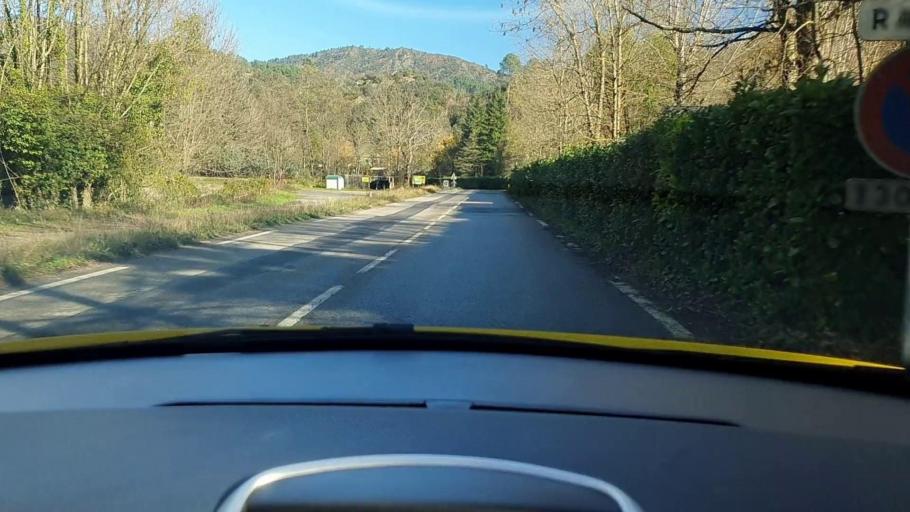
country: FR
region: Languedoc-Roussillon
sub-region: Departement du Gard
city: Lasalle
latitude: 44.1123
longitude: 3.7704
